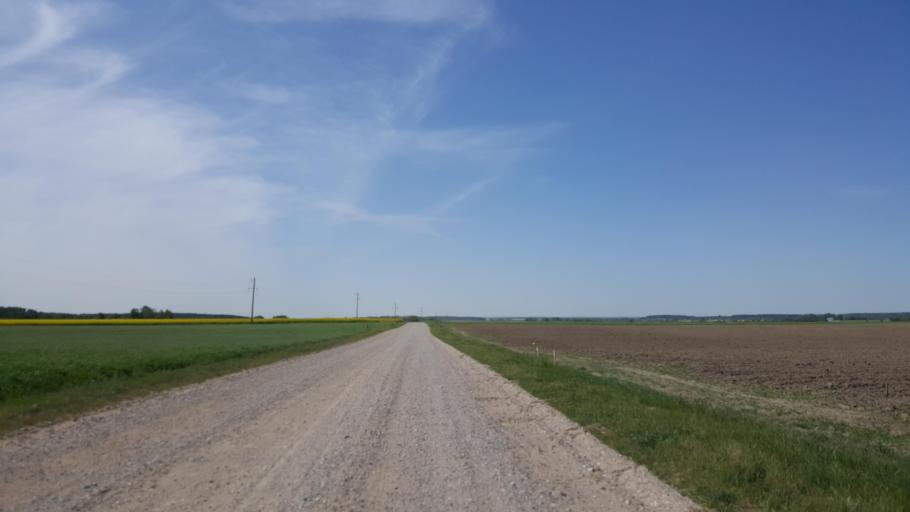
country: BY
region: Brest
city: Charnawchytsy
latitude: 52.2368
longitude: 23.6544
